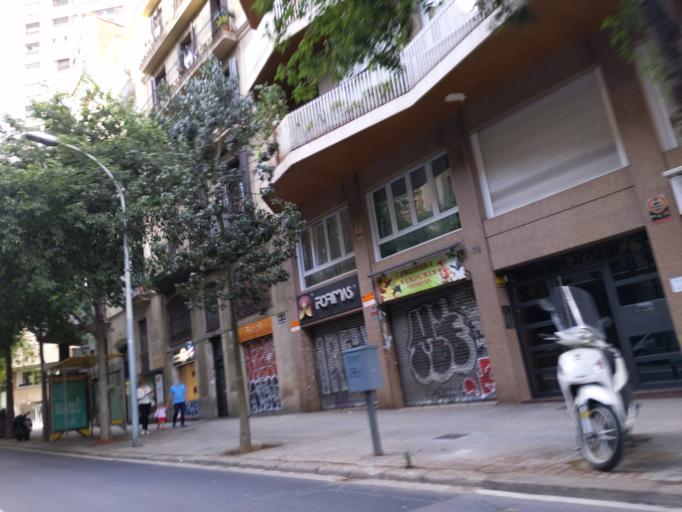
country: ES
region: Catalonia
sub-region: Provincia de Barcelona
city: Barcelona
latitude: 41.3859
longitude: 2.1582
